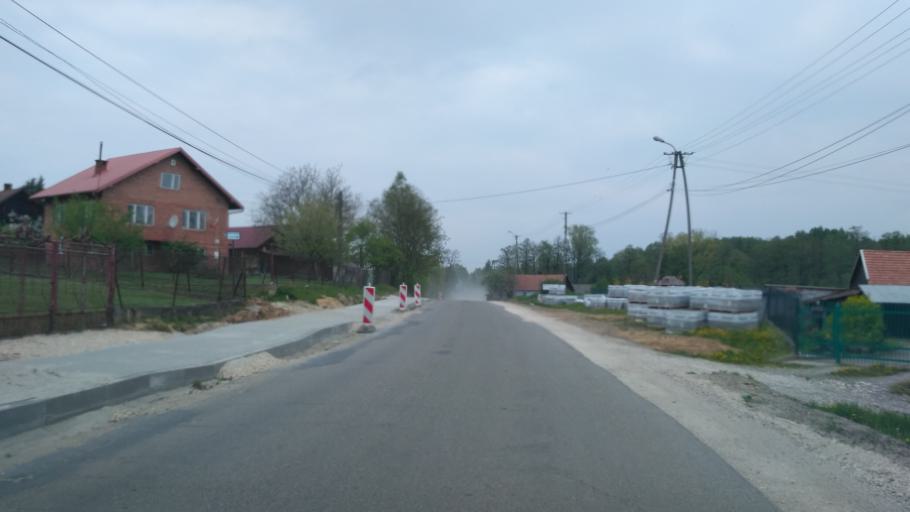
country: PL
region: Lesser Poland Voivodeship
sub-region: Powiat tarnowski
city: Skrzyszow
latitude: 49.9801
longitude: 21.0652
